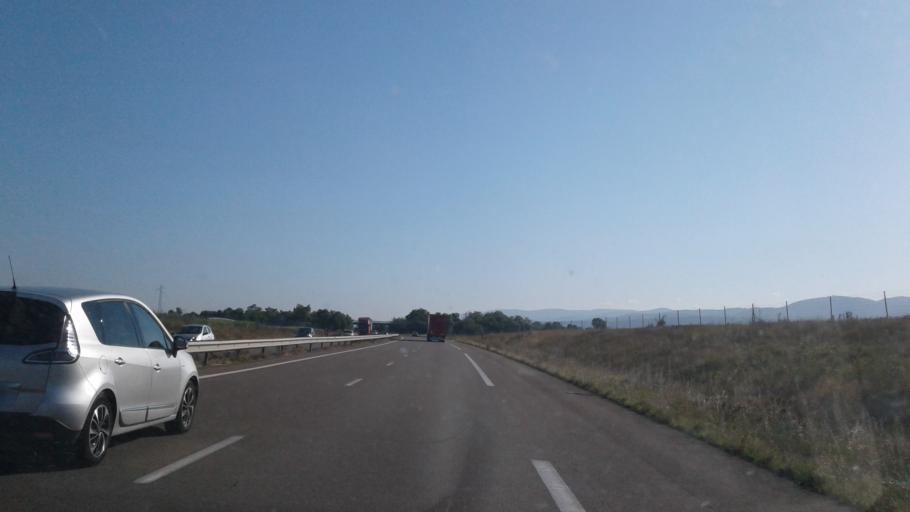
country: FR
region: Rhone-Alpes
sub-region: Departement de l'Ain
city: Leyment
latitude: 45.9424
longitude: 5.2936
